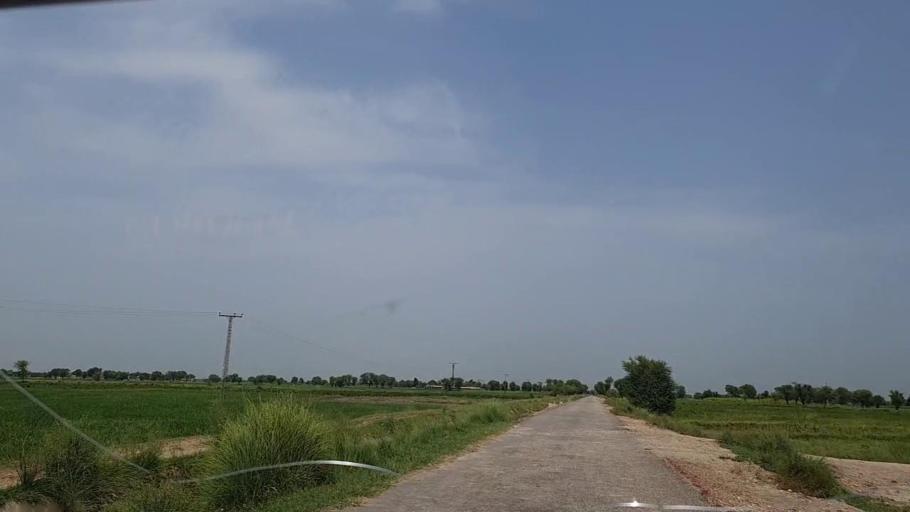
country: PK
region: Sindh
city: Tharu Shah
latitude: 26.9316
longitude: 68.0684
